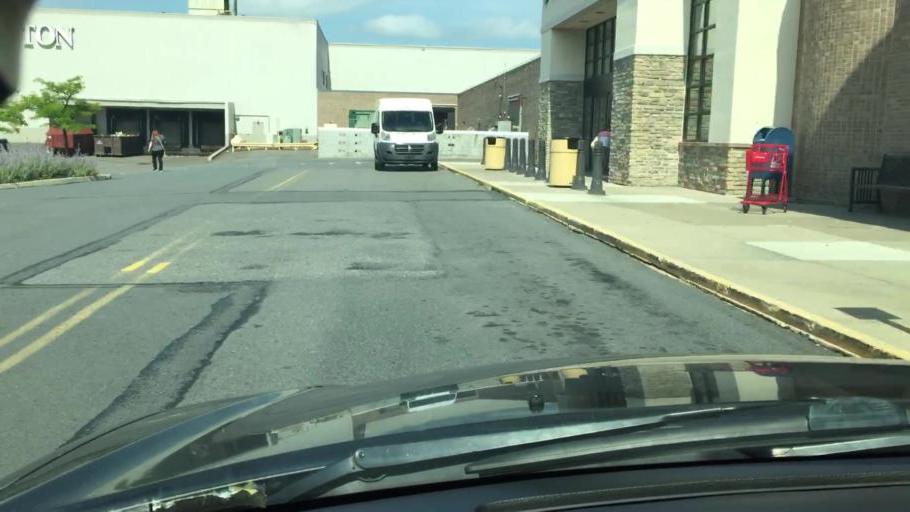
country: US
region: Pennsylvania
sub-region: Luzerne County
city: Georgetown
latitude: 41.2453
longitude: -75.8461
